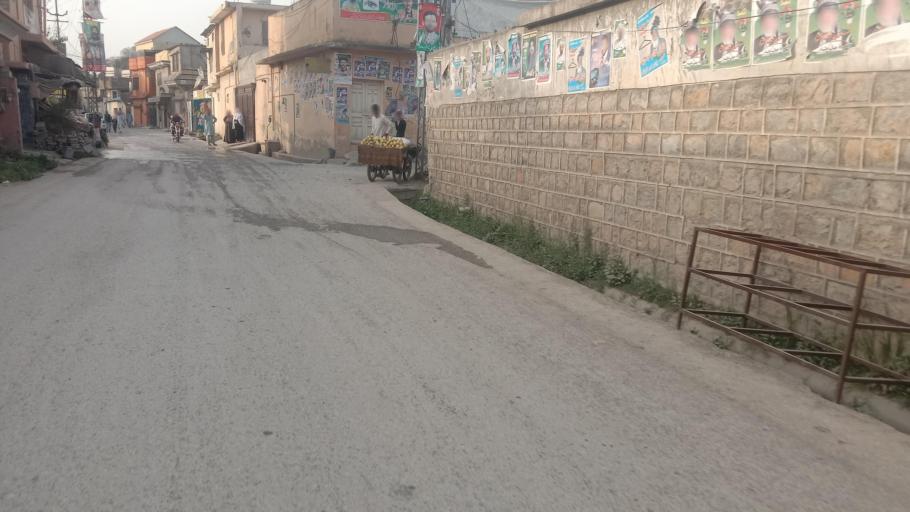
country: PK
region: Khyber Pakhtunkhwa
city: Abbottabad
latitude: 34.1729
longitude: 73.2568
